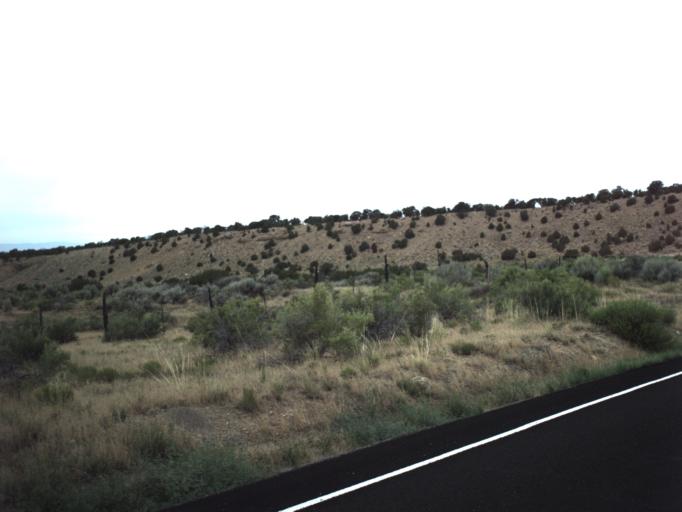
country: US
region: Utah
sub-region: Carbon County
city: East Carbon City
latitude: 39.4811
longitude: -110.4010
